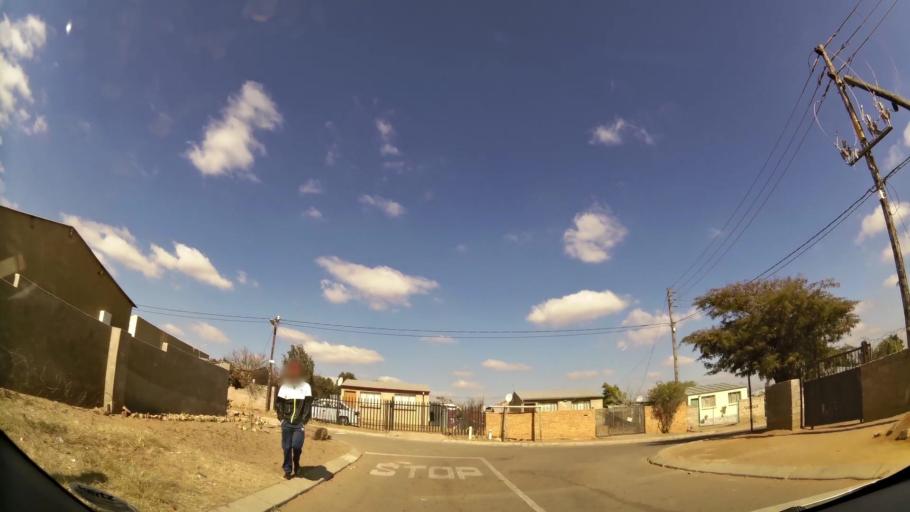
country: ZA
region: Gauteng
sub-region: West Rand District Municipality
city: Krugersdorp
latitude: -26.1441
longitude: 27.7870
